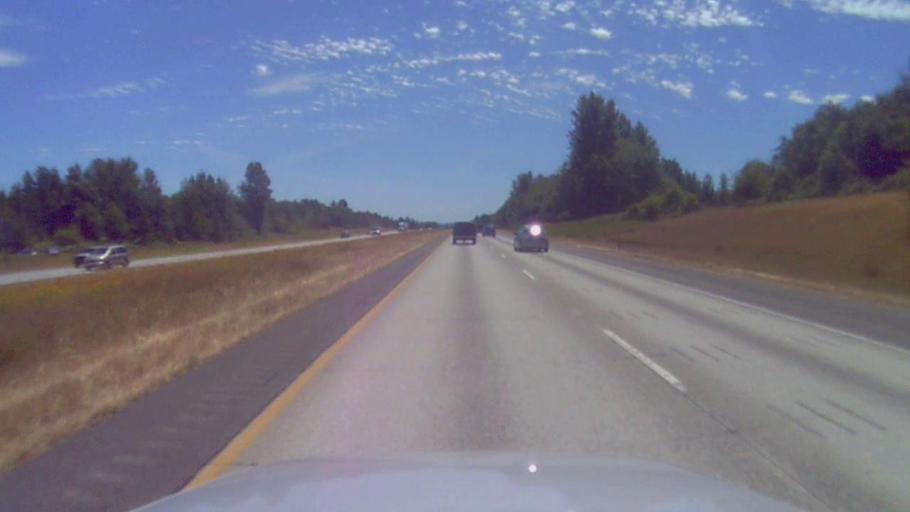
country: US
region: Washington
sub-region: Whatcom County
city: Marietta-Alderwood
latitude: 48.8096
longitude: -122.5410
